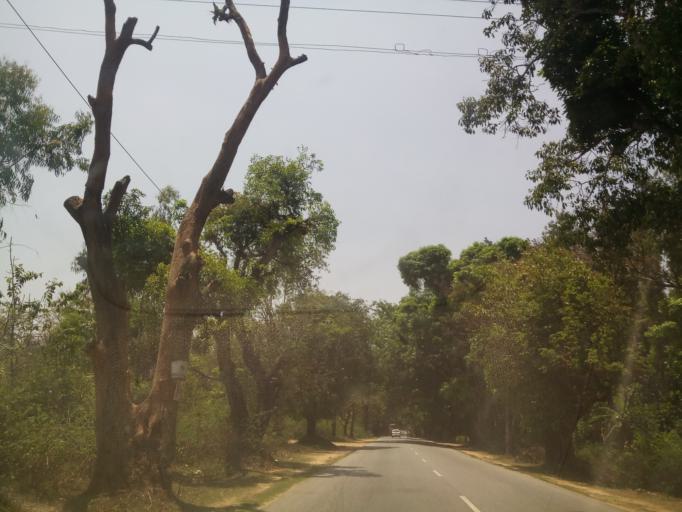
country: IN
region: Karnataka
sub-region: Hassan
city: Alur
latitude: 12.9506
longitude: 75.9067
